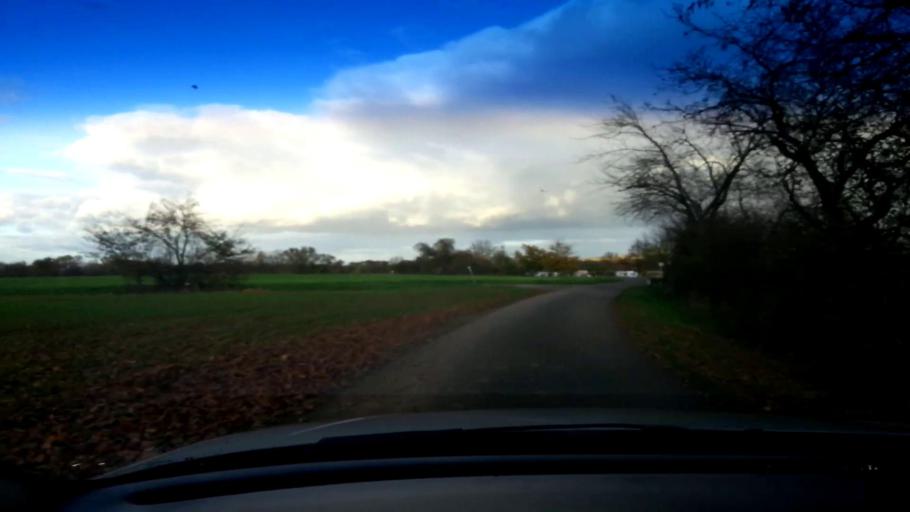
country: DE
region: Bavaria
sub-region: Upper Franconia
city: Zapfendorf
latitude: 50.0447
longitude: 10.9323
